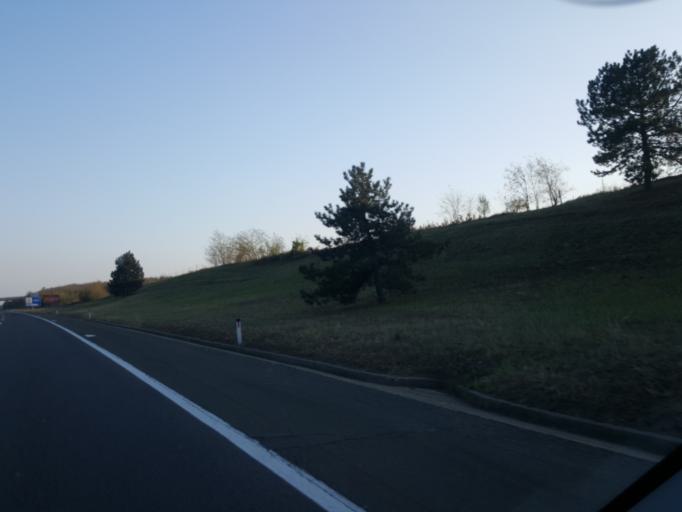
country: RS
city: Lugavcina
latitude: 44.4879
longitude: 21.0254
